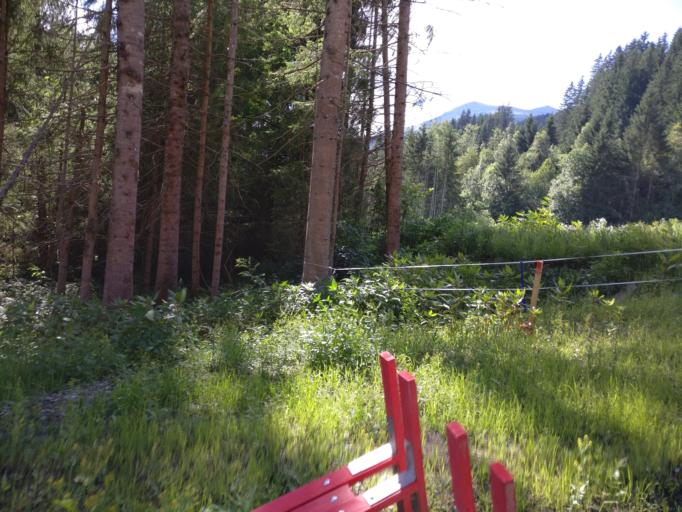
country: AT
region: Salzburg
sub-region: Politischer Bezirk Zell am See
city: Neukirchen am Grossvenediger
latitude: 47.2507
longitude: 12.2614
